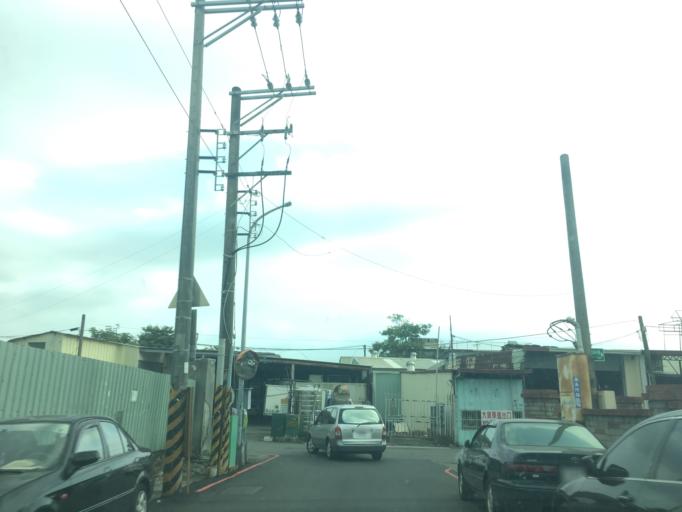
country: TW
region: Taiwan
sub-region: Taichung City
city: Taichung
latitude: 24.1661
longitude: 120.7017
